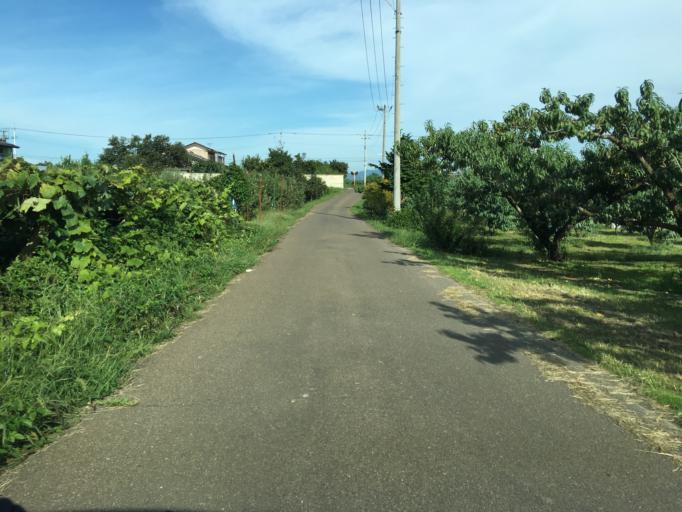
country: JP
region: Fukushima
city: Hobaramachi
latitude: 37.8175
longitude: 140.5224
